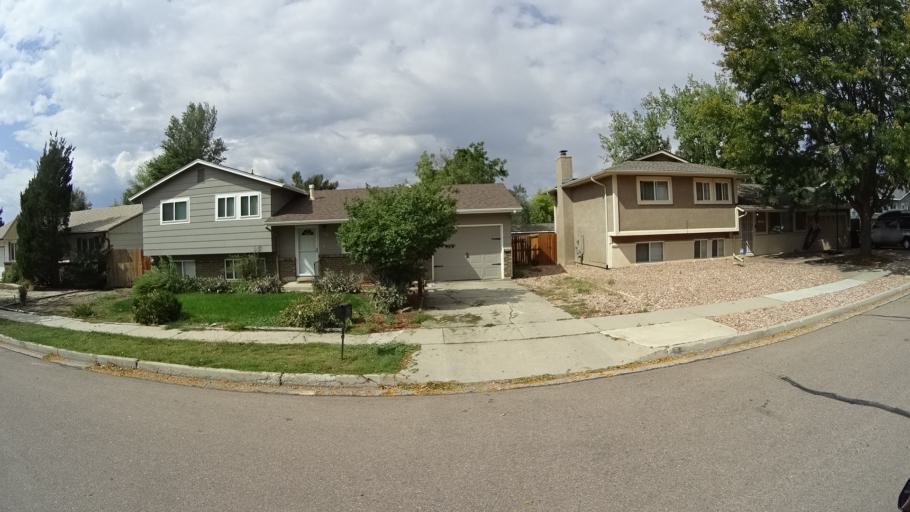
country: US
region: Colorado
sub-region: El Paso County
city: Cimarron Hills
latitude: 38.8514
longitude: -104.7366
